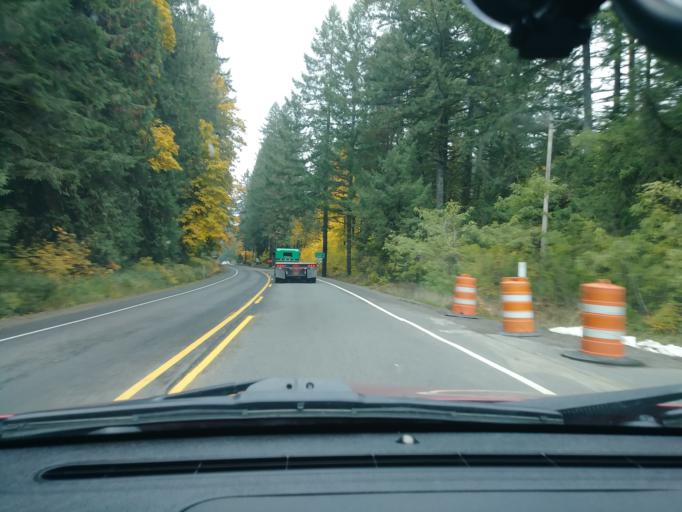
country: US
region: Oregon
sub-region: Washington County
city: Banks
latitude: 45.6506
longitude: -123.2762
